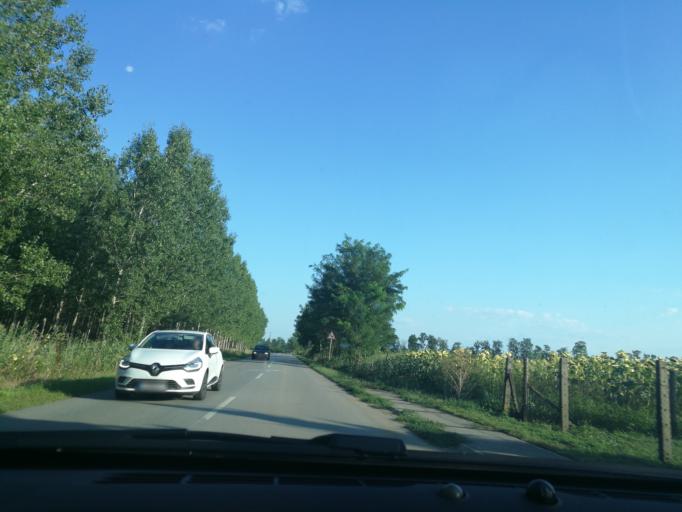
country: HU
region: Szabolcs-Szatmar-Bereg
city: Buj
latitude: 48.1229
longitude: 21.6461
